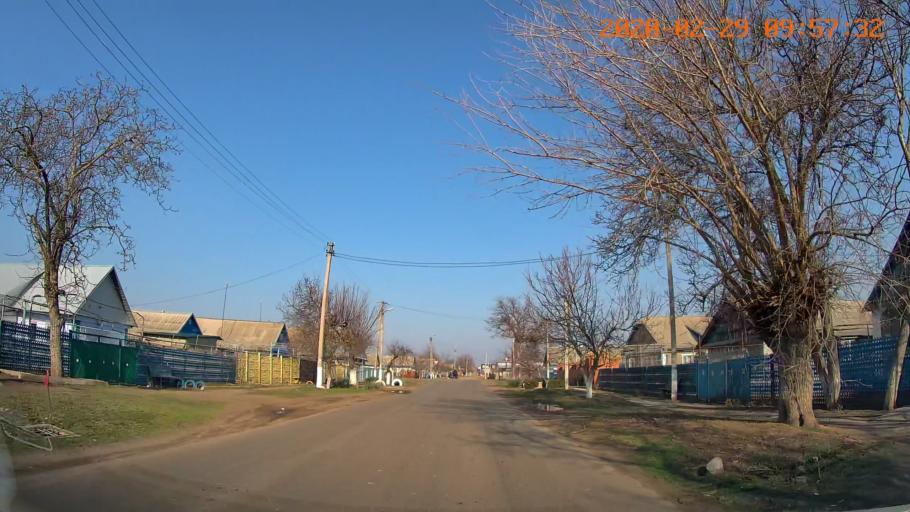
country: MD
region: Telenesti
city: Slobozia
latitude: 46.7511
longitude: 29.6983
